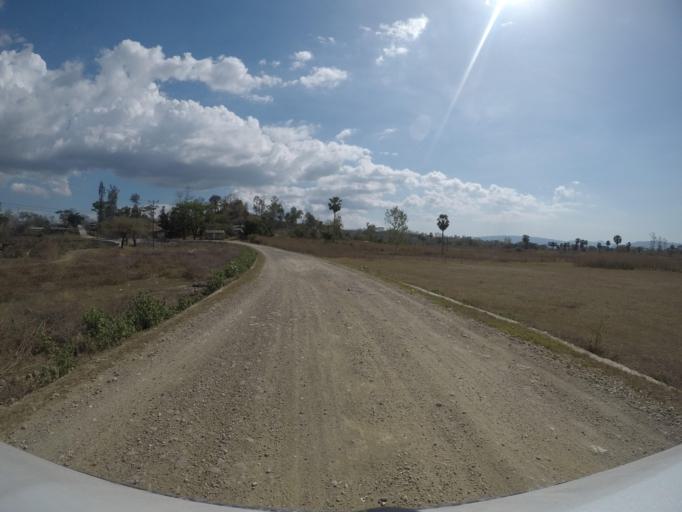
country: TL
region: Bobonaro
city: Maliana
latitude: -8.9980
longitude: 125.1972
